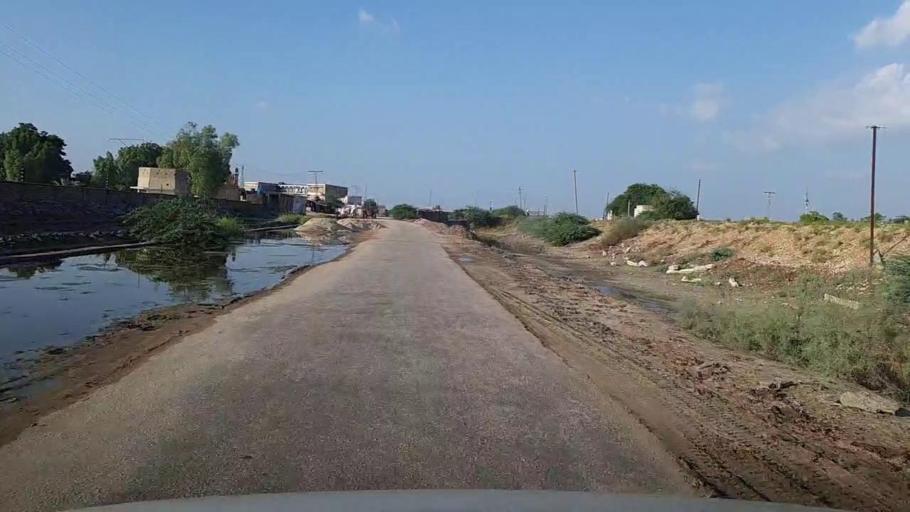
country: PK
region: Sindh
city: Hingorja
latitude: 27.0917
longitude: 68.4152
